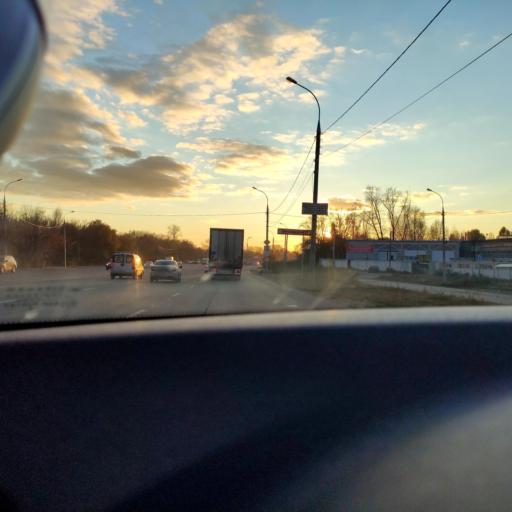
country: RU
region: Samara
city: Smyshlyayevka
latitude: 53.2522
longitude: 50.3624
